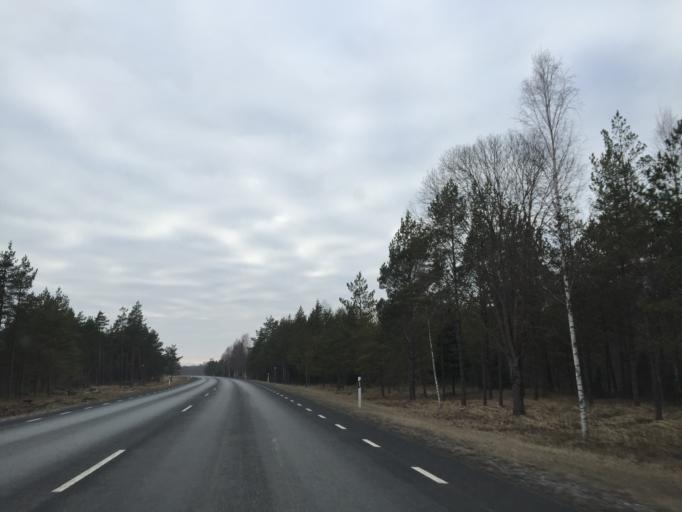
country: EE
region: Saare
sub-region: Orissaare vald
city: Orissaare
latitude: 58.5324
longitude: 22.9703
